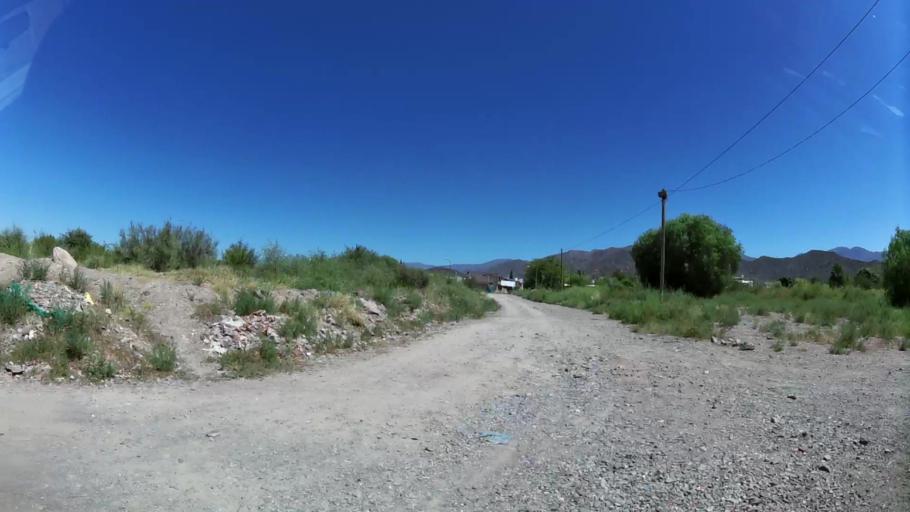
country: AR
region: Mendoza
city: Las Heras
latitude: -32.8388
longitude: -68.8637
